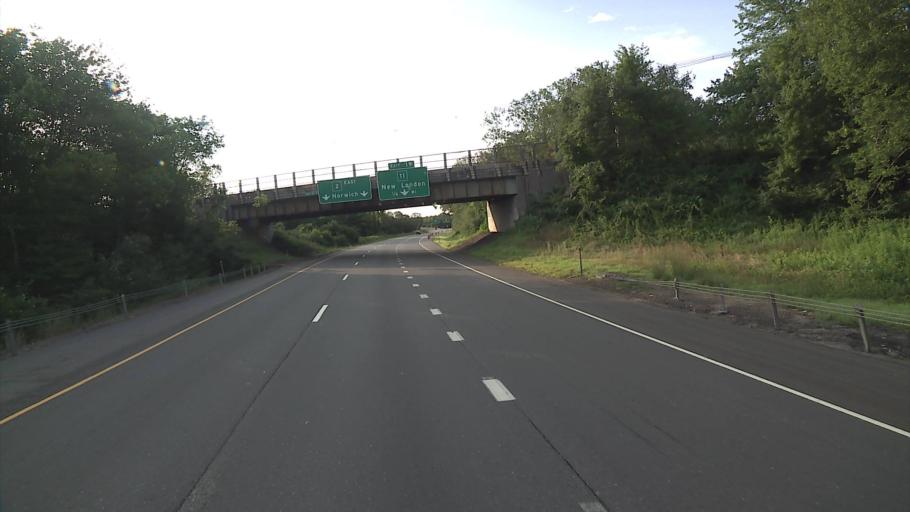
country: US
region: Connecticut
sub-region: New London County
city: Colchester
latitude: 41.5667
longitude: -72.3320
